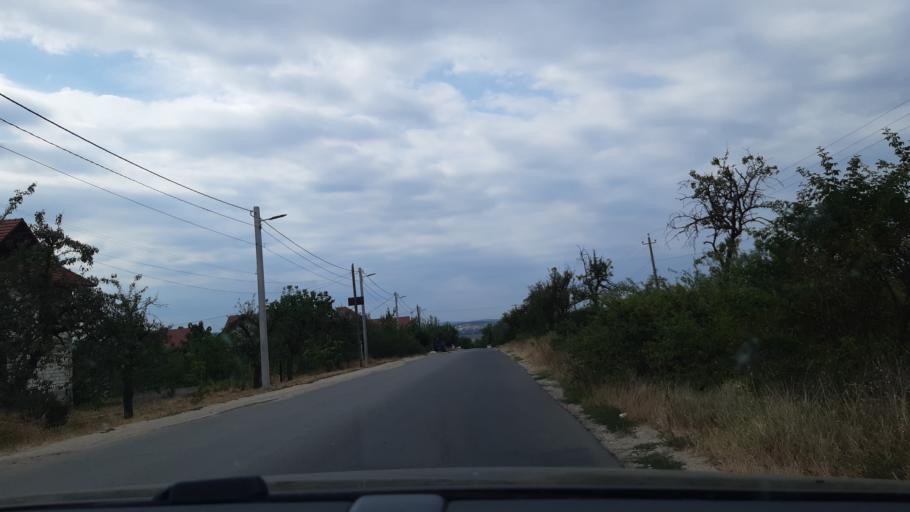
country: MD
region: Chisinau
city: Vatra
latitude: 47.0472
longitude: 28.7416
